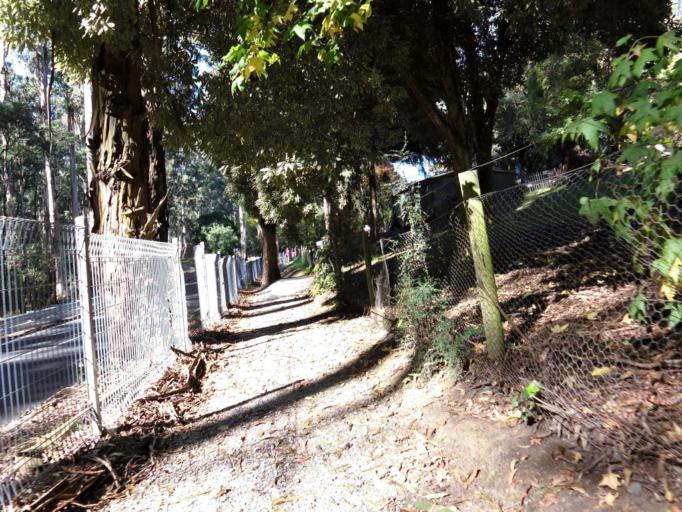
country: AU
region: Victoria
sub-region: Cardinia
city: Cockatoo
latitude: -37.9434
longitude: 145.4951
